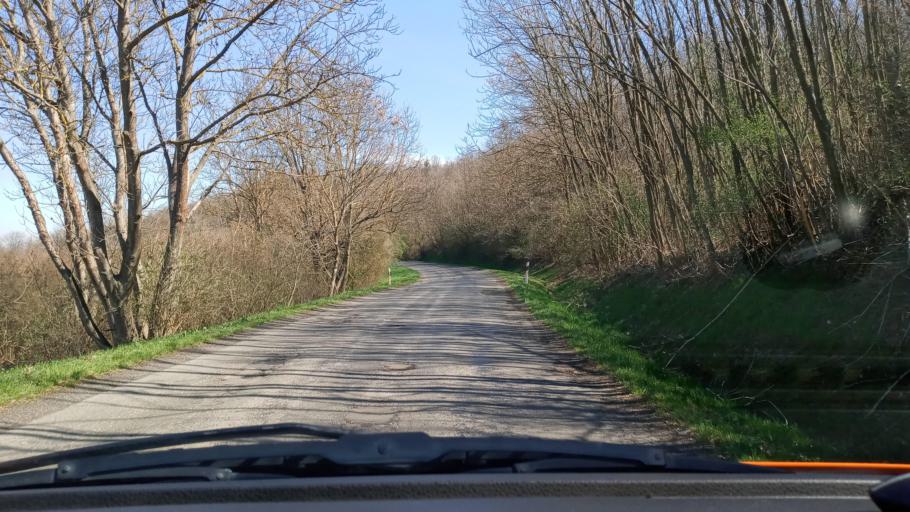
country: HU
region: Baranya
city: Boly
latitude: 46.0510
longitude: 18.4553
